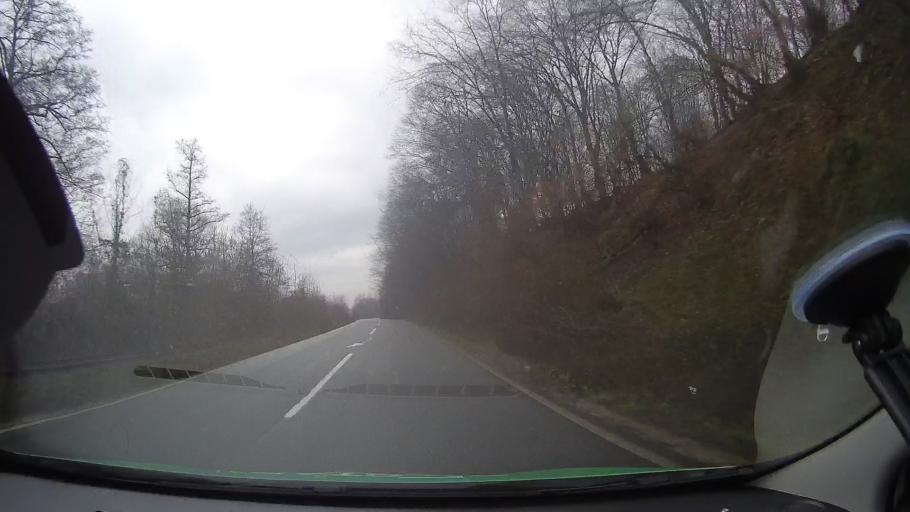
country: RO
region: Arad
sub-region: Comuna Almas
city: Almas
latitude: 46.3014
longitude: 22.2001
